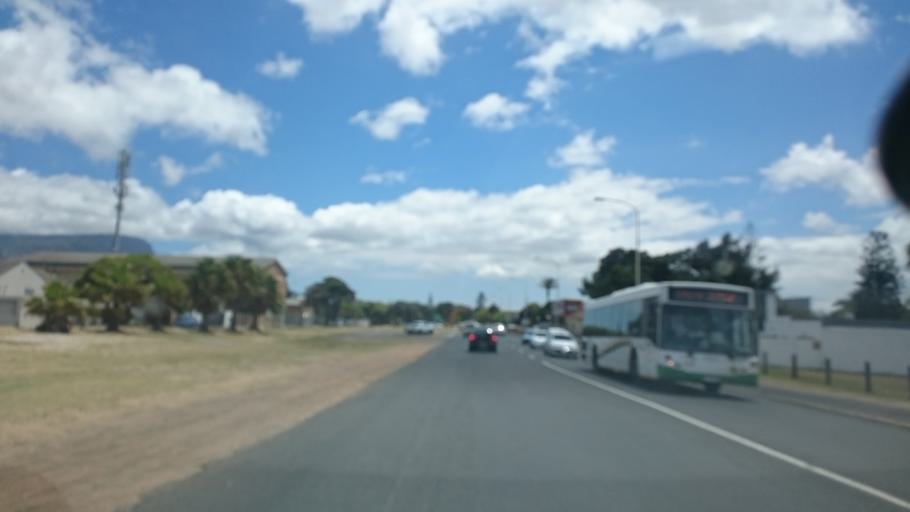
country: ZA
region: Western Cape
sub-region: City of Cape Town
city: Bergvliet
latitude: -34.0526
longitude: 18.4615
